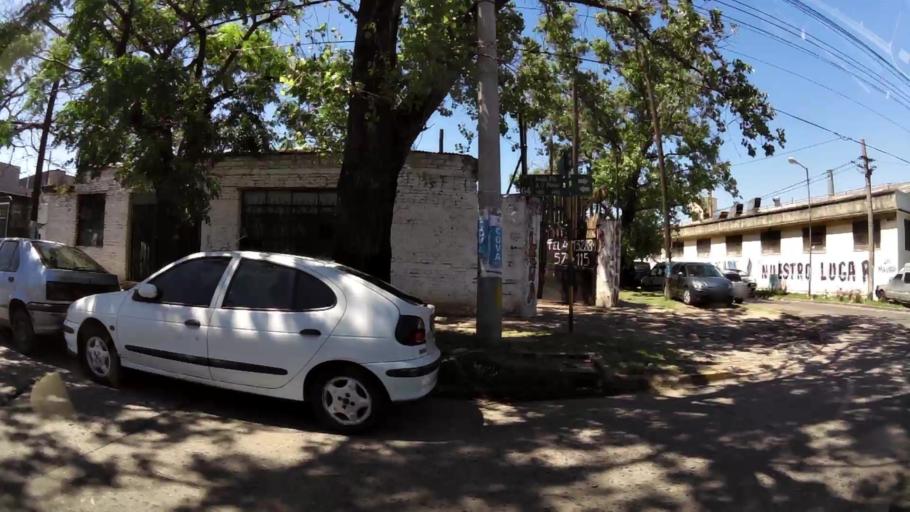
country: AR
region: Buenos Aires
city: Caseros
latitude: -34.5780
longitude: -58.5502
